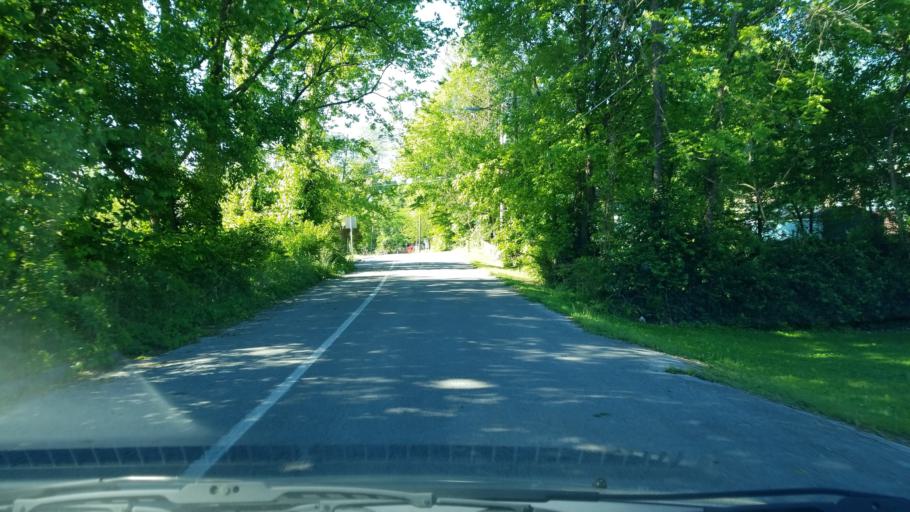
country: US
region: Tennessee
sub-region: Hamilton County
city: Lookout Mountain
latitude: 34.9930
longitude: -85.3300
